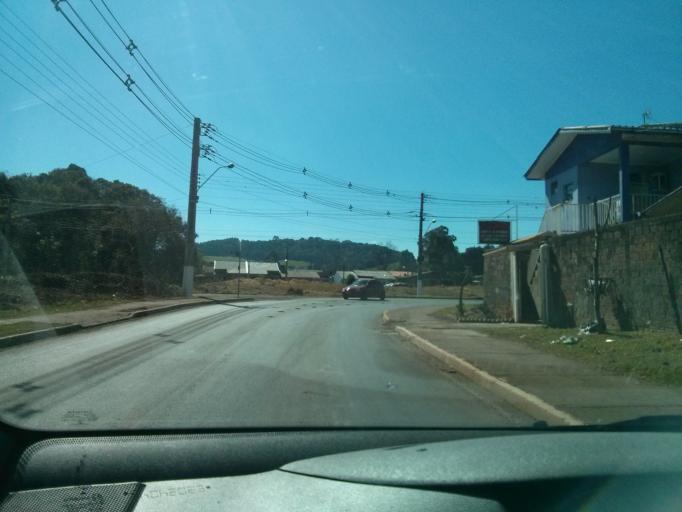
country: BR
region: Santa Catarina
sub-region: Chapeco
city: Chapeco
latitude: -27.0908
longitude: -52.6835
